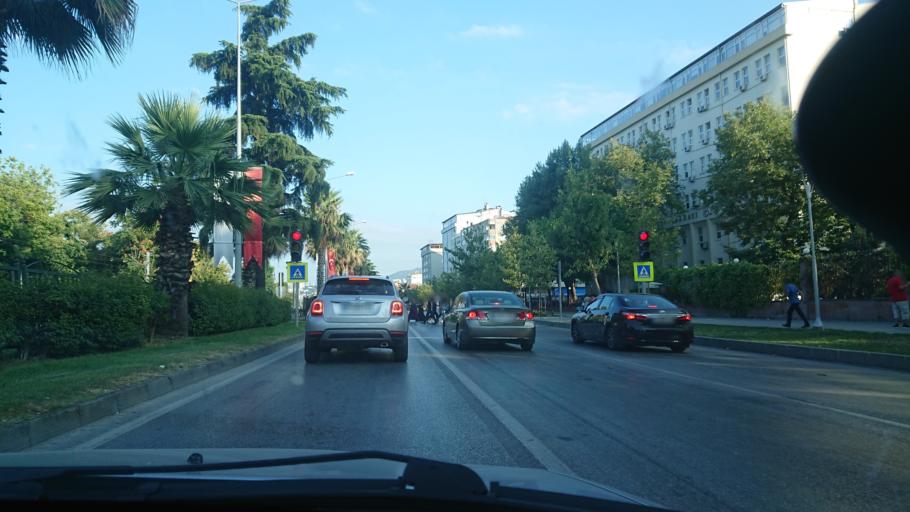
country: TR
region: Samsun
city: Samsun
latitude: 41.2890
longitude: 36.3375
